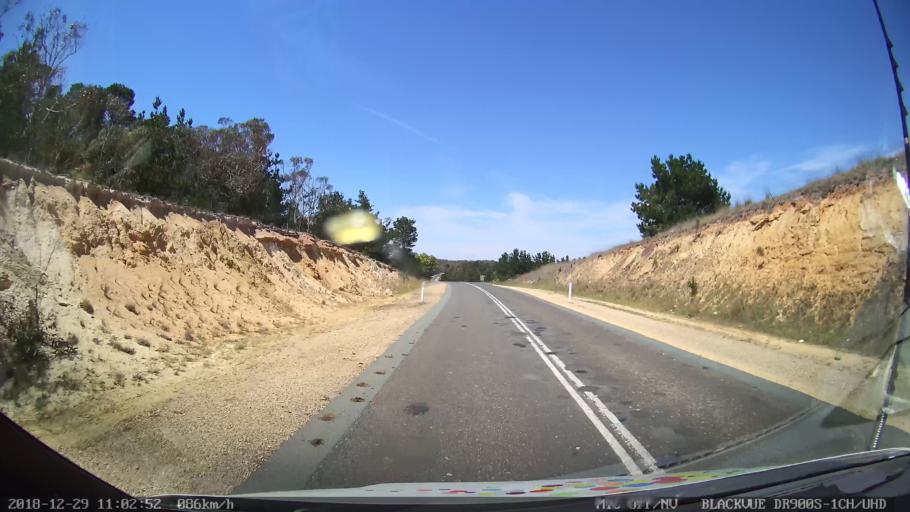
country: AU
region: New South Wales
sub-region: Palerang
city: Bungendore
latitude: -35.1740
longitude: 149.5549
